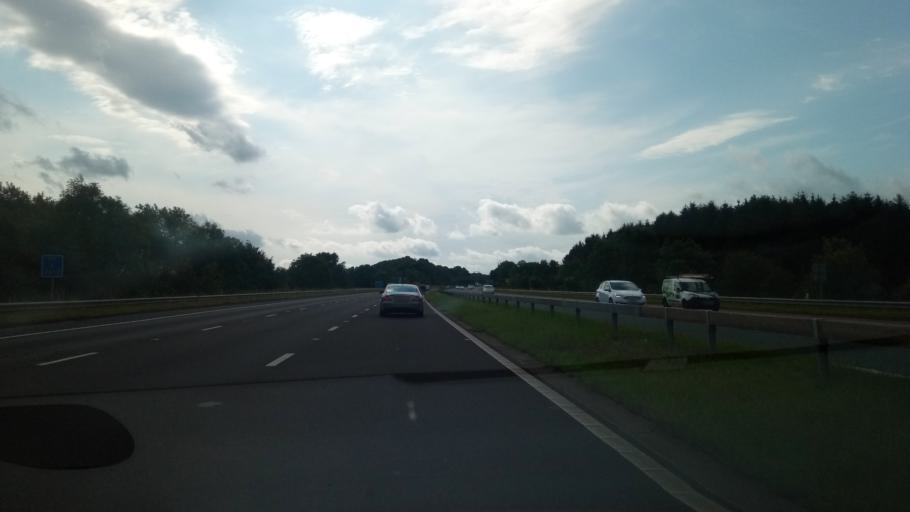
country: GB
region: England
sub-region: Cumbria
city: Penrith
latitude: 54.6414
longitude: -2.7349
